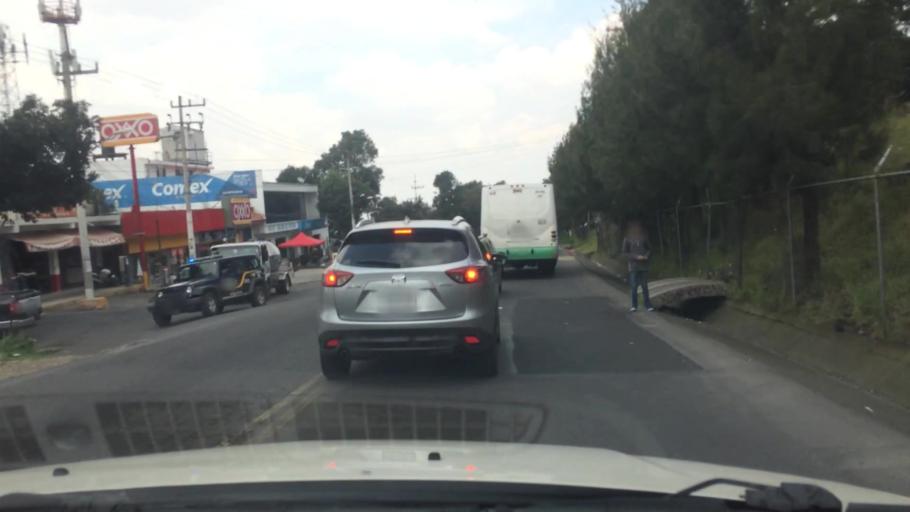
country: MX
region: Mexico City
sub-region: Tlalpan
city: Lomas de Tepemecatl
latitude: 19.2680
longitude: -99.2224
